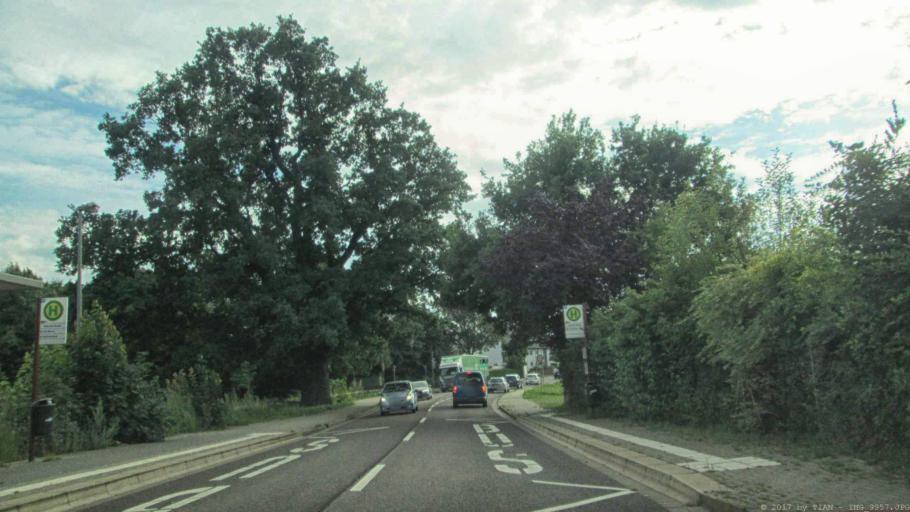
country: DE
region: Lower Saxony
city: Wolfsburg
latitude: 52.3951
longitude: 10.7282
